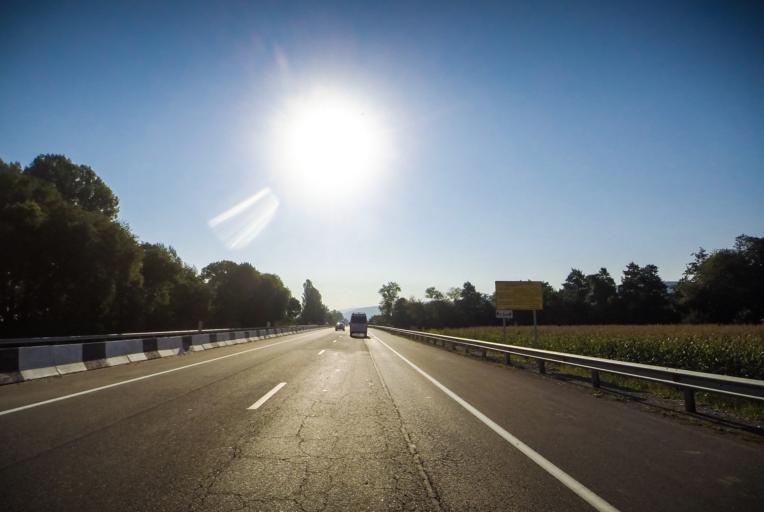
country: RU
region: North Ossetia
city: Zmeyskaya
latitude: 43.3229
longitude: 44.1225
